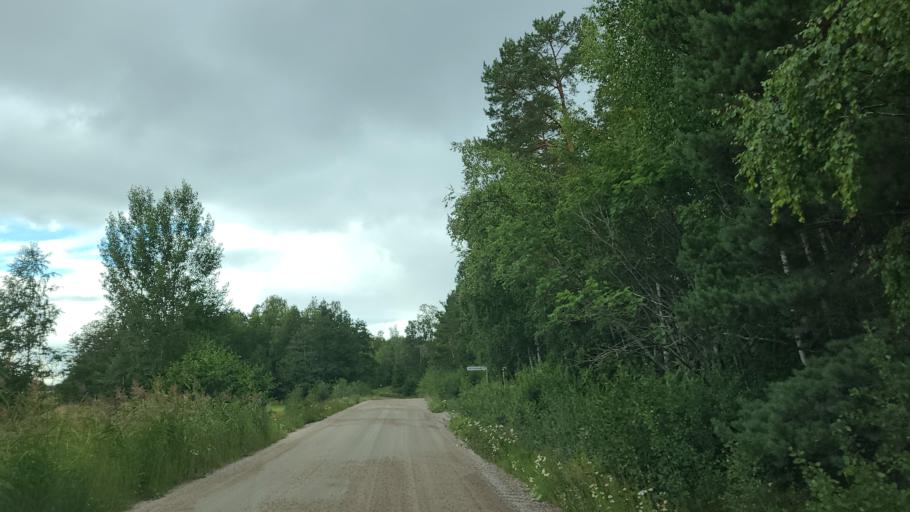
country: FI
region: Varsinais-Suomi
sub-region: Aboland-Turunmaa
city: Nagu
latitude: 60.2058
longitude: 21.8414
